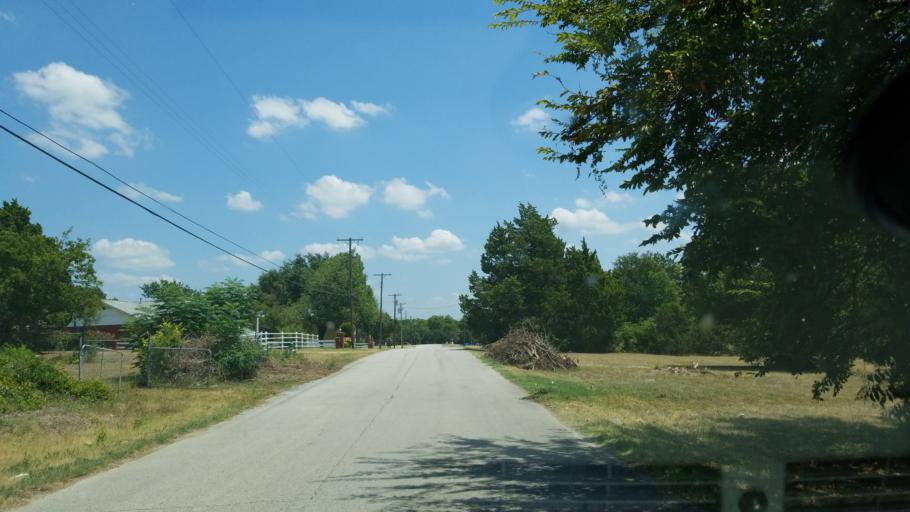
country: US
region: Texas
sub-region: Dallas County
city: Duncanville
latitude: 32.6719
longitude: -96.8942
